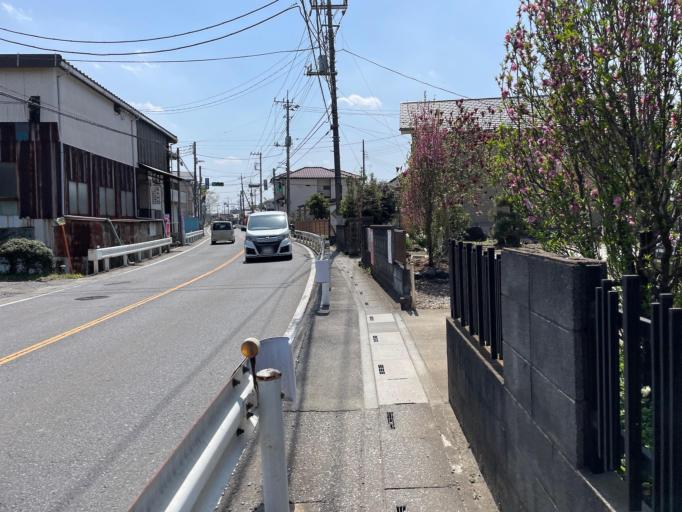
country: JP
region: Saitama
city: Sayama
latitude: 35.8712
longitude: 139.4047
